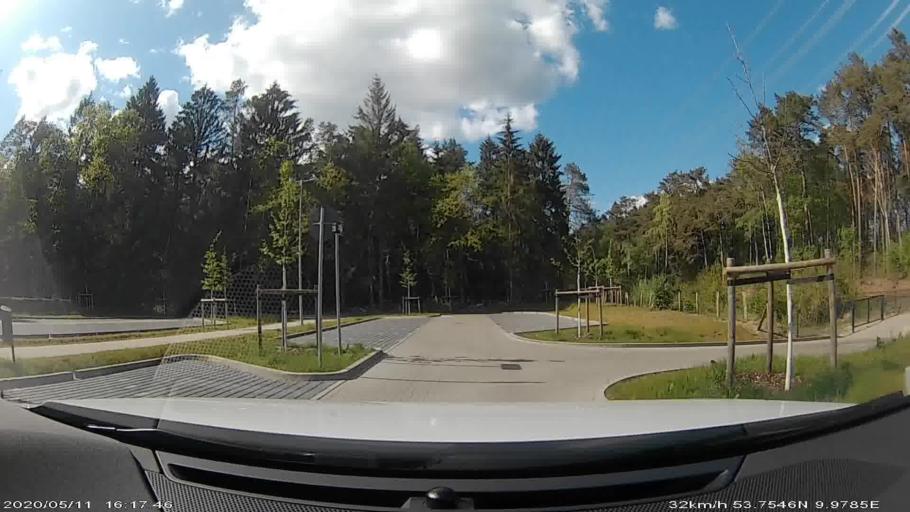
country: DE
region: Schleswig-Holstein
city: Henstedt-Ulzburg
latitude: 53.7541
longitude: 9.9792
